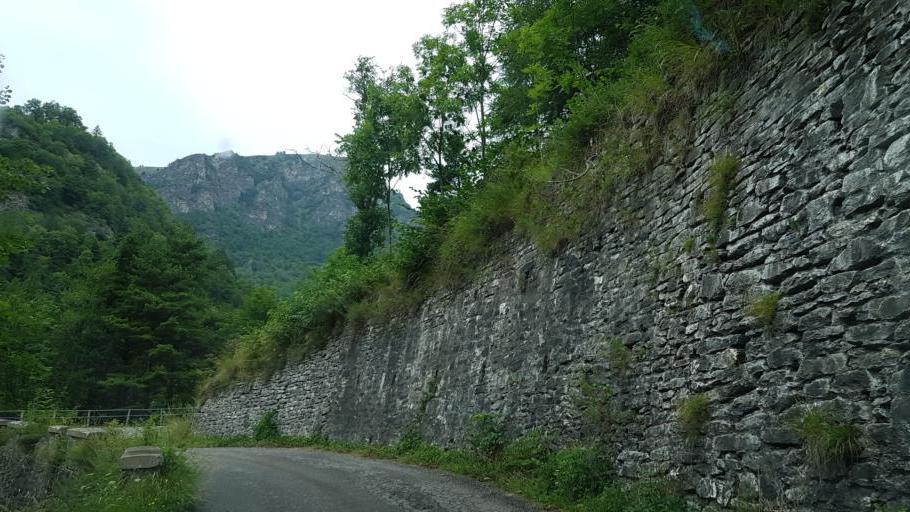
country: IT
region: Piedmont
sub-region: Provincia di Cuneo
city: Stroppo
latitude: 44.5132
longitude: 7.1261
